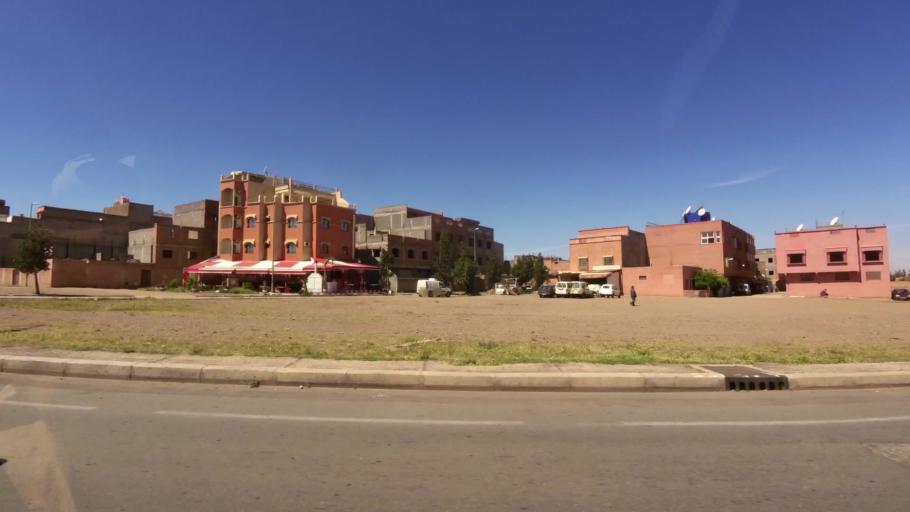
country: MA
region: Marrakech-Tensift-Al Haouz
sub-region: Marrakech
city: Marrakesh
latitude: 31.5754
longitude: -7.9816
